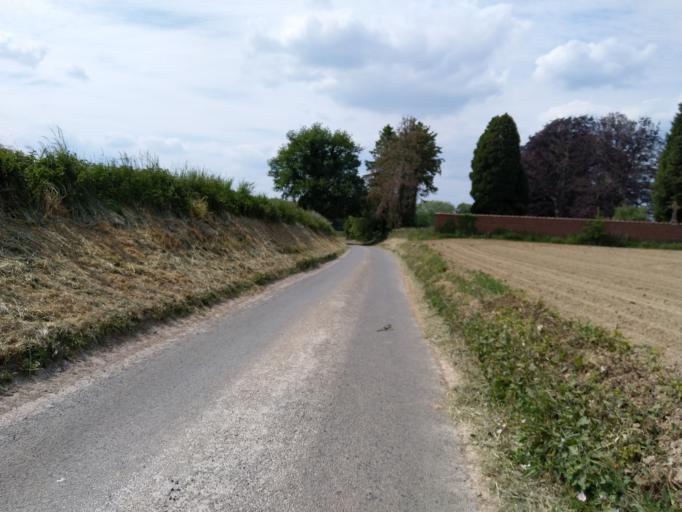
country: BE
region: Wallonia
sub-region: Province du Hainaut
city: Silly
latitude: 50.5961
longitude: 3.9456
